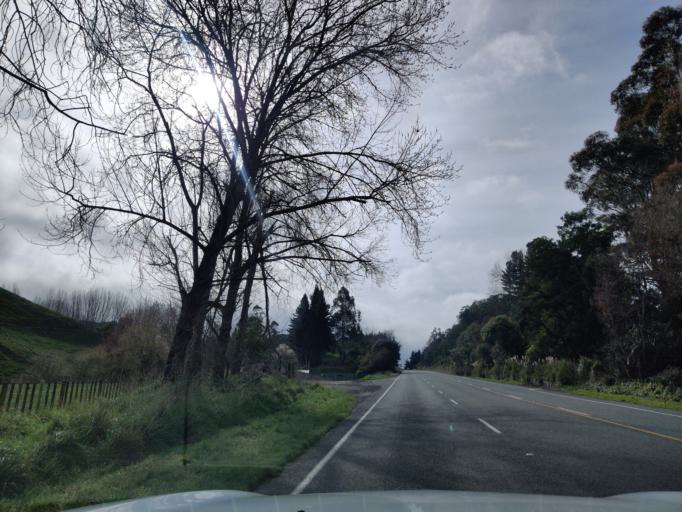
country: NZ
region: Manawatu-Wanganui
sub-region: Ruapehu District
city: Waiouru
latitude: -39.7733
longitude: 175.7928
